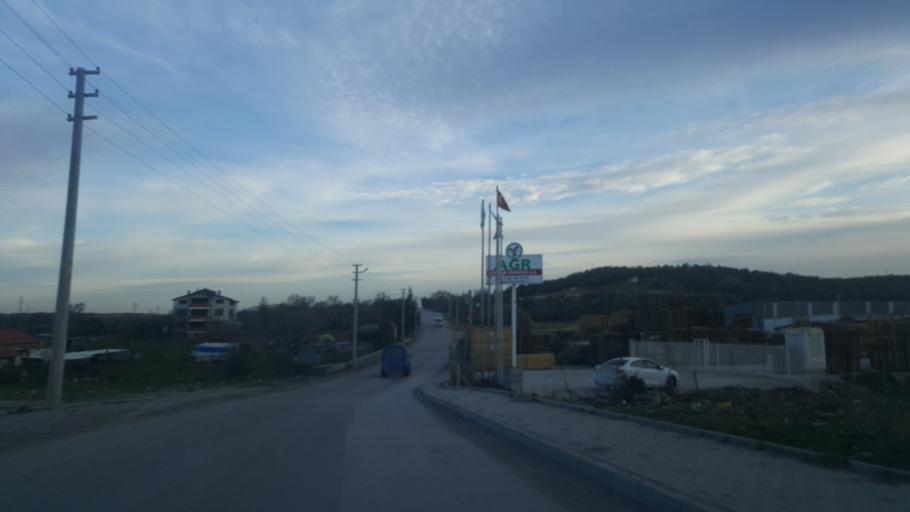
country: TR
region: Kocaeli
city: Tavsanli
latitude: 40.8492
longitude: 29.5550
